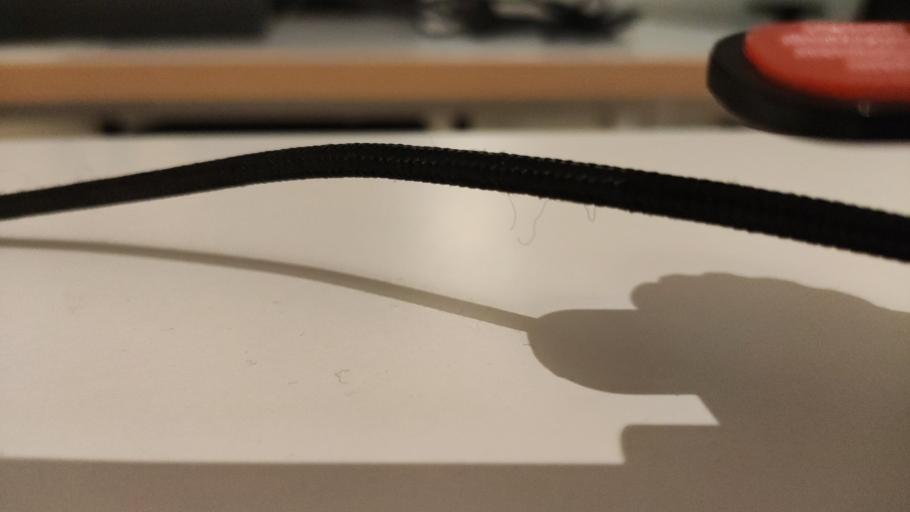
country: RU
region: Moskovskaya
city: Kurovskoye
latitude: 55.5971
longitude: 38.9245
